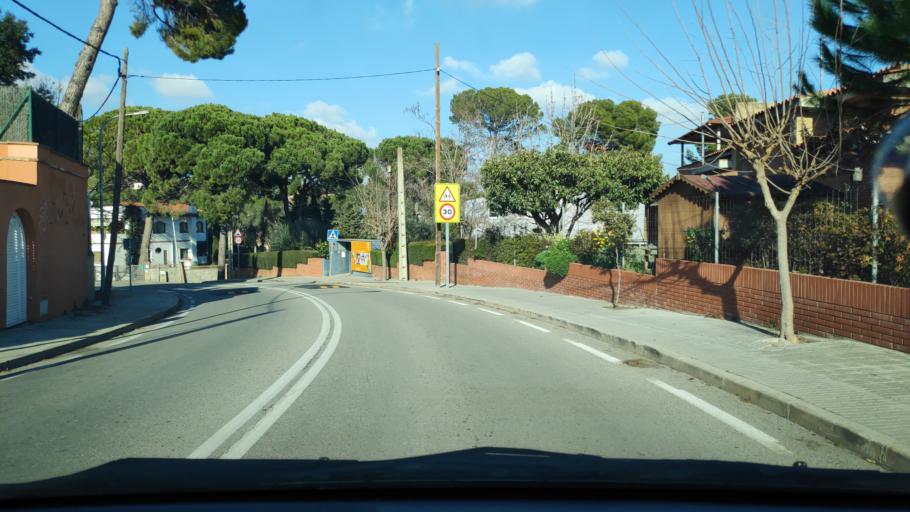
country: ES
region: Catalonia
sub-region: Provincia de Barcelona
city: Sant Cugat del Valles
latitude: 41.4986
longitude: 2.0883
